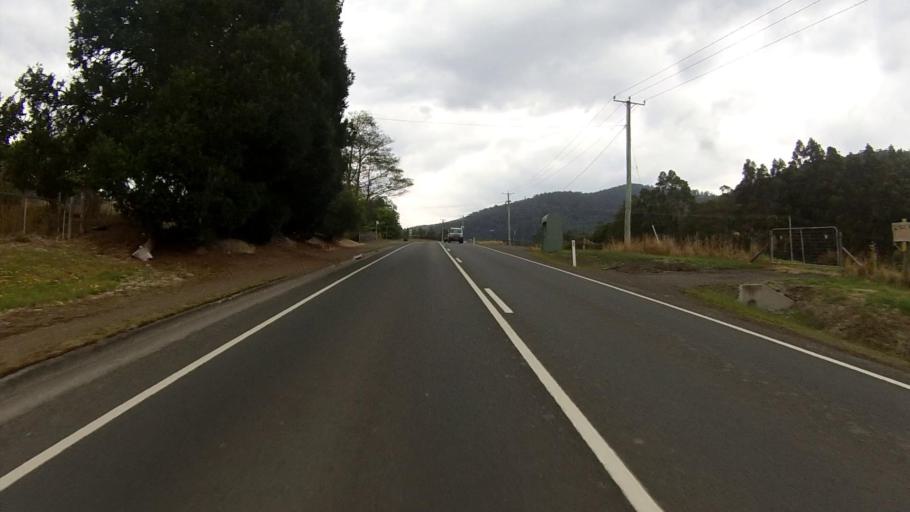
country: AU
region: Tasmania
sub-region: Huon Valley
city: Cygnet
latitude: -43.1505
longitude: 147.0699
